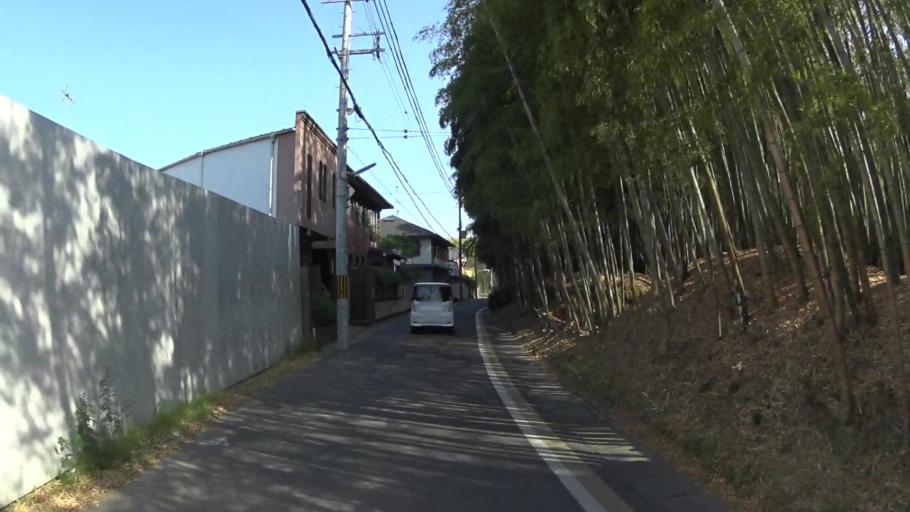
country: JP
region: Kyoto
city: Muko
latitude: 34.9528
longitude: 135.6758
